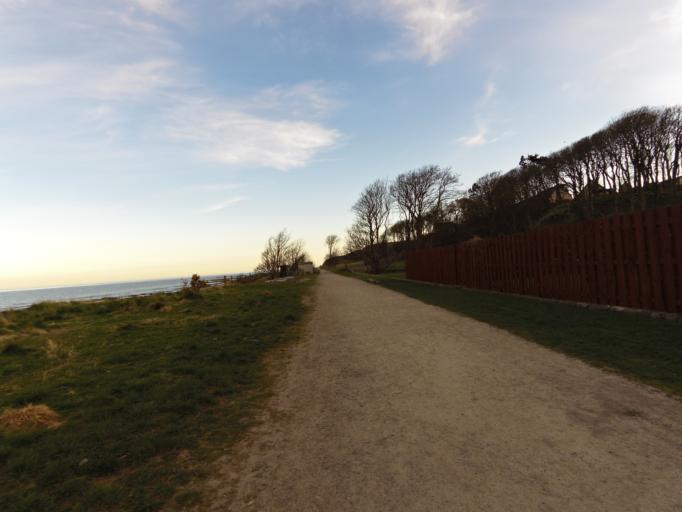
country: GB
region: Scotland
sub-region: Aberdeenshire
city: Inverbervie
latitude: 56.8404
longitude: -2.2761
